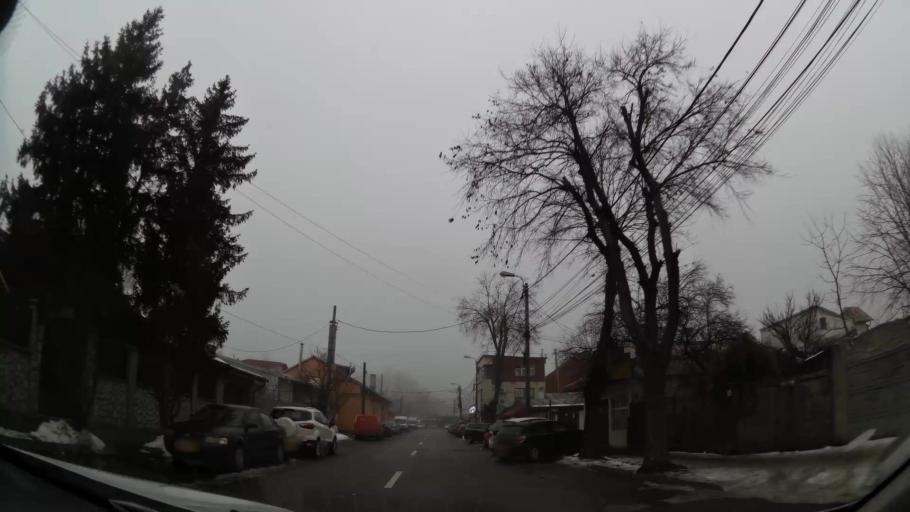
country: RO
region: Ilfov
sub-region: Comuna Chiajna
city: Rosu
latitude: 44.4836
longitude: 26.0332
